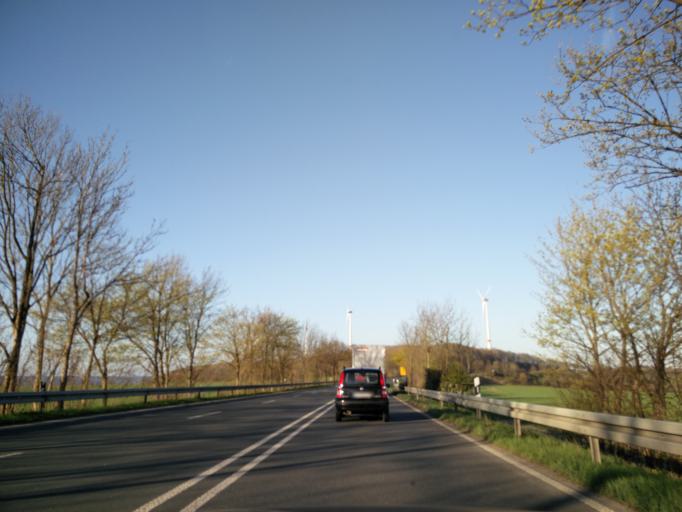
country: DE
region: North Rhine-Westphalia
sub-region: Regierungsbezirk Detmold
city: Altenbeken
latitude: 51.7284
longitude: 8.9140
